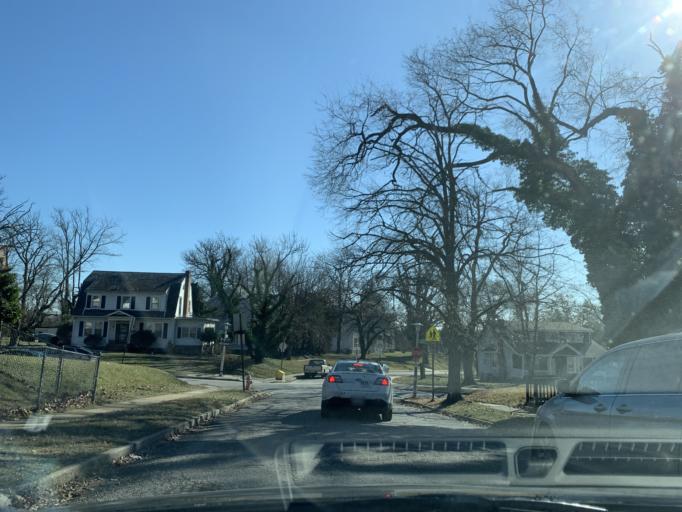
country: US
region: Maryland
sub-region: Baltimore County
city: Woodlawn
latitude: 39.3167
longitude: -76.6843
